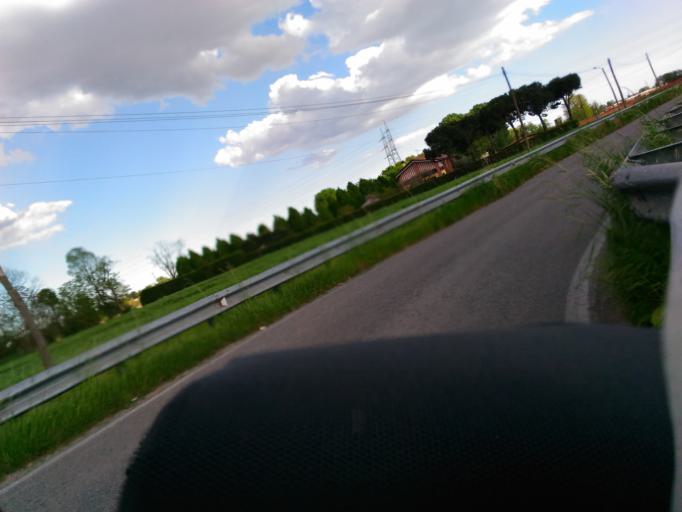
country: IT
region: Lombardy
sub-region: Citta metropolitana di Milano
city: San Giuliano Milanese
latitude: 45.4005
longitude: 9.2994
